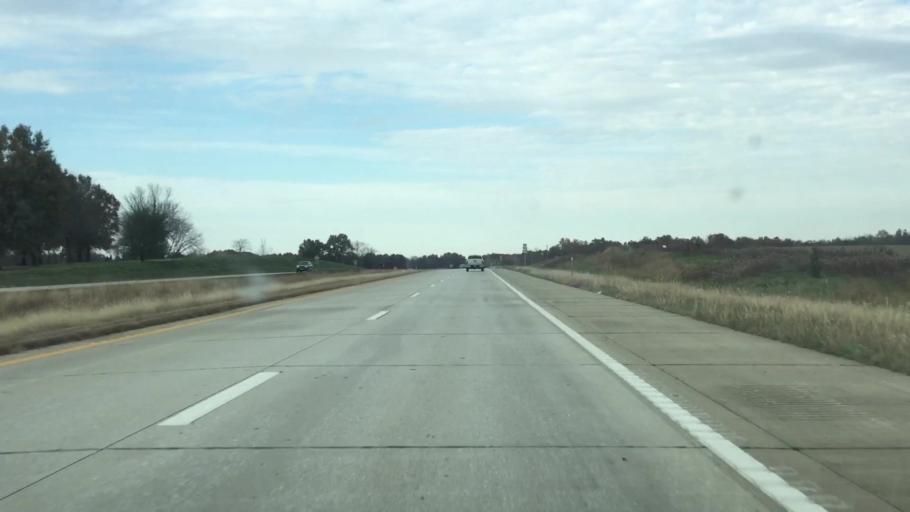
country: US
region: Missouri
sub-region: Henry County
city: Clinton
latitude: 38.3475
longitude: -93.7567
